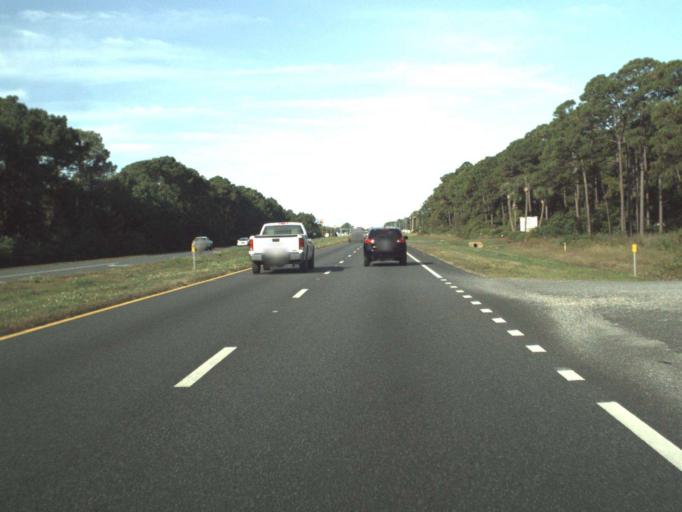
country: US
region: Florida
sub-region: Walton County
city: Miramar Beach
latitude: 30.3850
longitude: -86.3704
